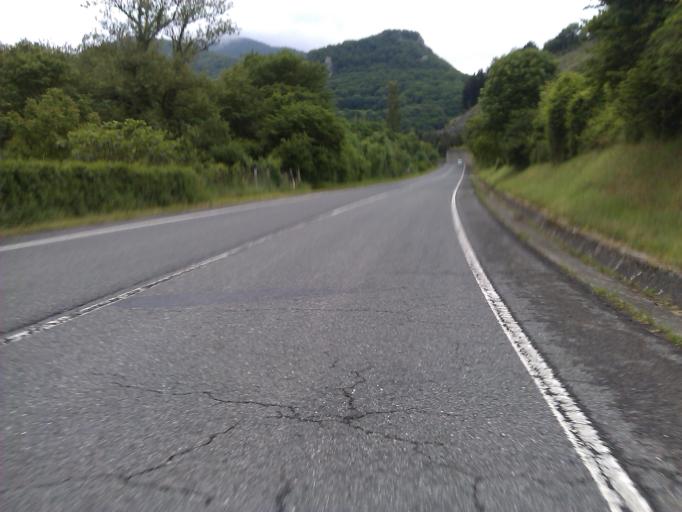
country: ES
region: Navarre
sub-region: Provincia de Navarra
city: Irurtzun
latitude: 42.9581
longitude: -1.8251
